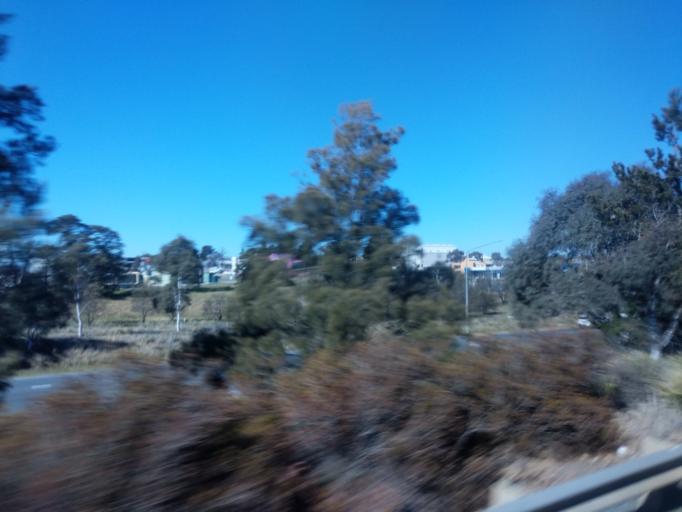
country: AU
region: Australian Capital Territory
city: Forrest
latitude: -35.3215
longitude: 149.1681
